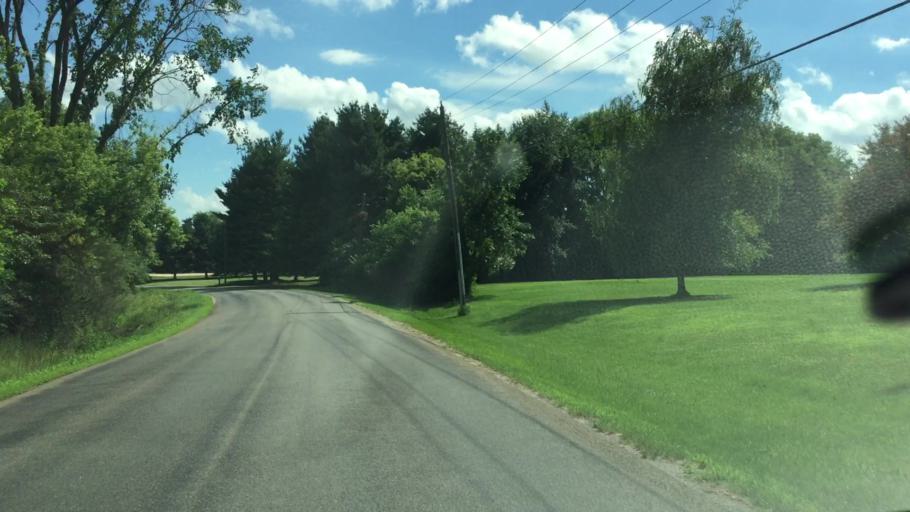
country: US
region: Iowa
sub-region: Linn County
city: Ely
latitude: 41.8246
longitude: -91.6242
